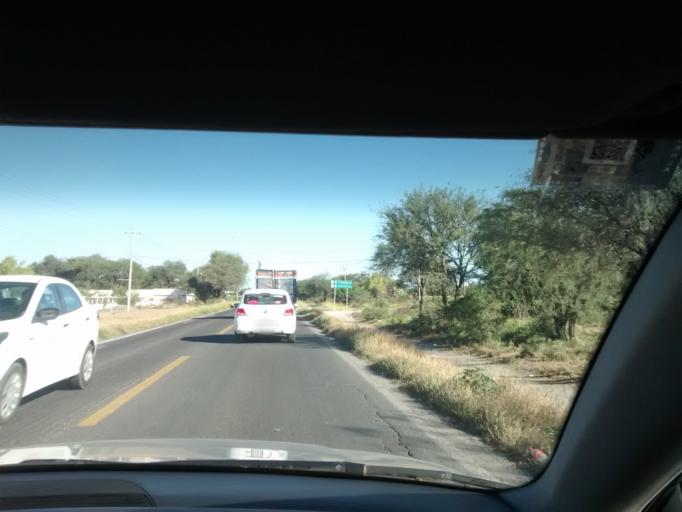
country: MX
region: Puebla
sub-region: Tehuacan
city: Magdalena Cuayucatepec
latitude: 18.5209
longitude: -97.5071
